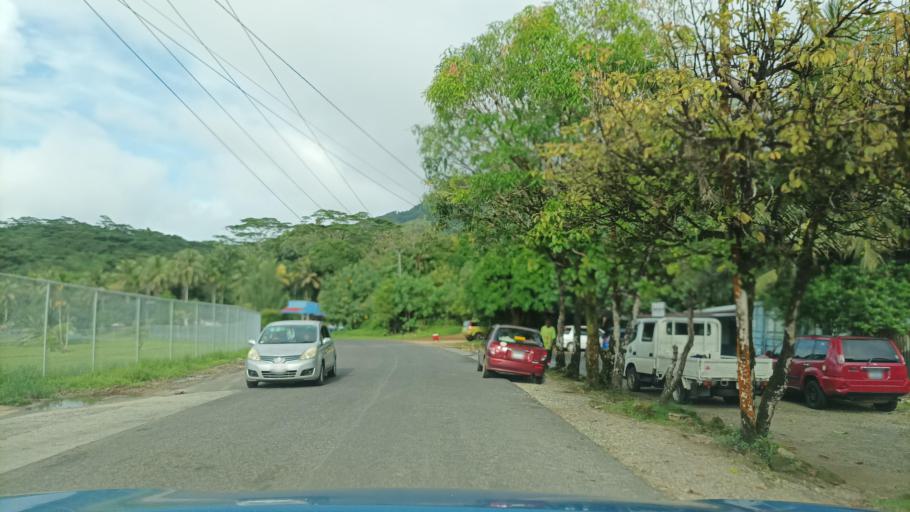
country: FM
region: Pohnpei
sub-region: Sokehs Municipality
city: Palikir - National Government Center
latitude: 6.9085
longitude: 158.1607
